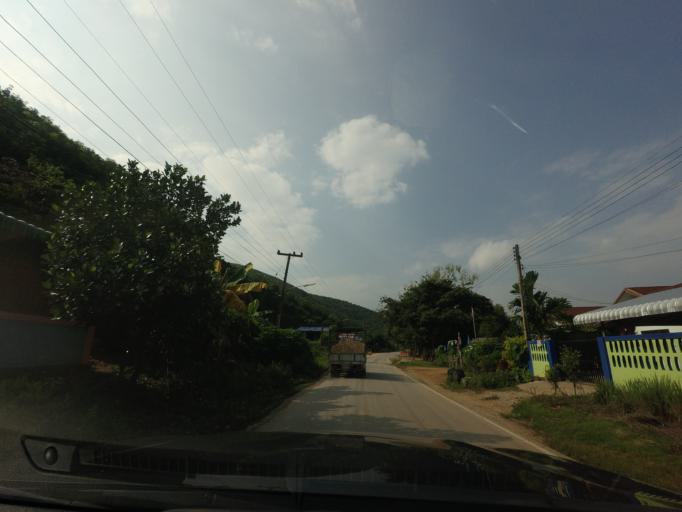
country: TH
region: Loei
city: Chiang Khan
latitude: 17.8410
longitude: 101.5681
